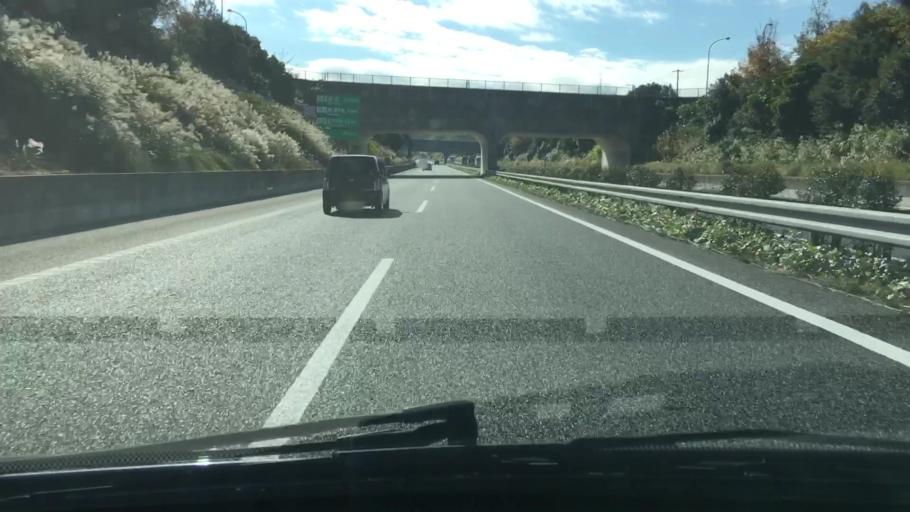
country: JP
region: Chiba
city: Kisarazu
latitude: 35.3442
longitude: 139.9445
